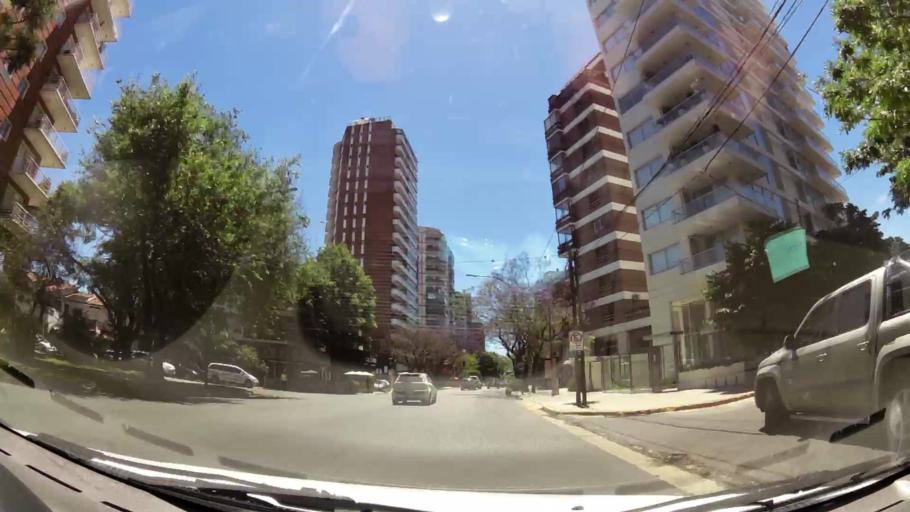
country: AR
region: Buenos Aires
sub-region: Partido de Vicente Lopez
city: Olivos
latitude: -34.4948
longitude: -58.4847
